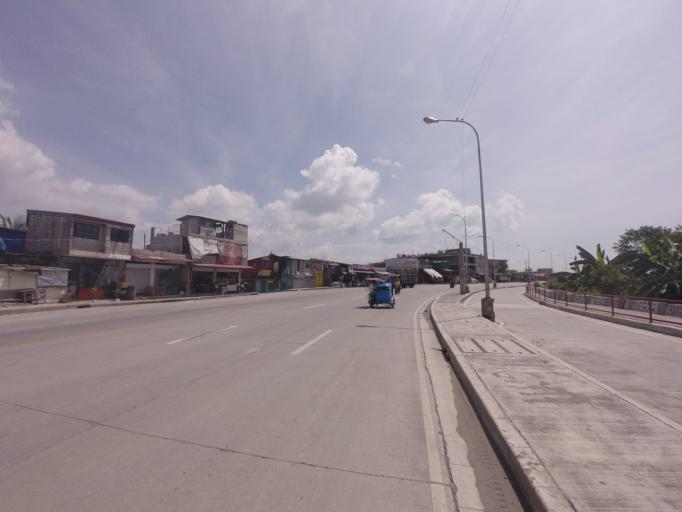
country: PH
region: Calabarzon
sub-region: Province of Rizal
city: Taguig
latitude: 14.5329
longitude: 121.1079
